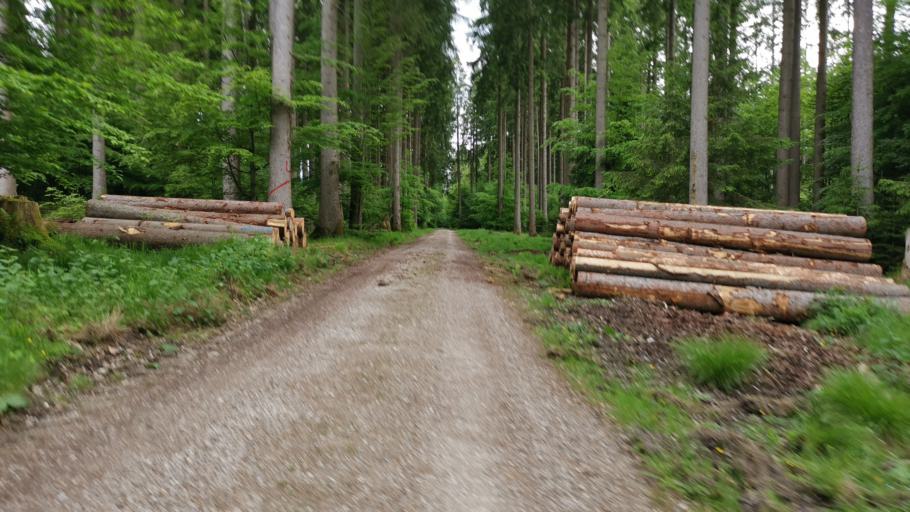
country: DE
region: Bavaria
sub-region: Upper Bavaria
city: Baierbrunn
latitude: 48.0277
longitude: 11.4580
